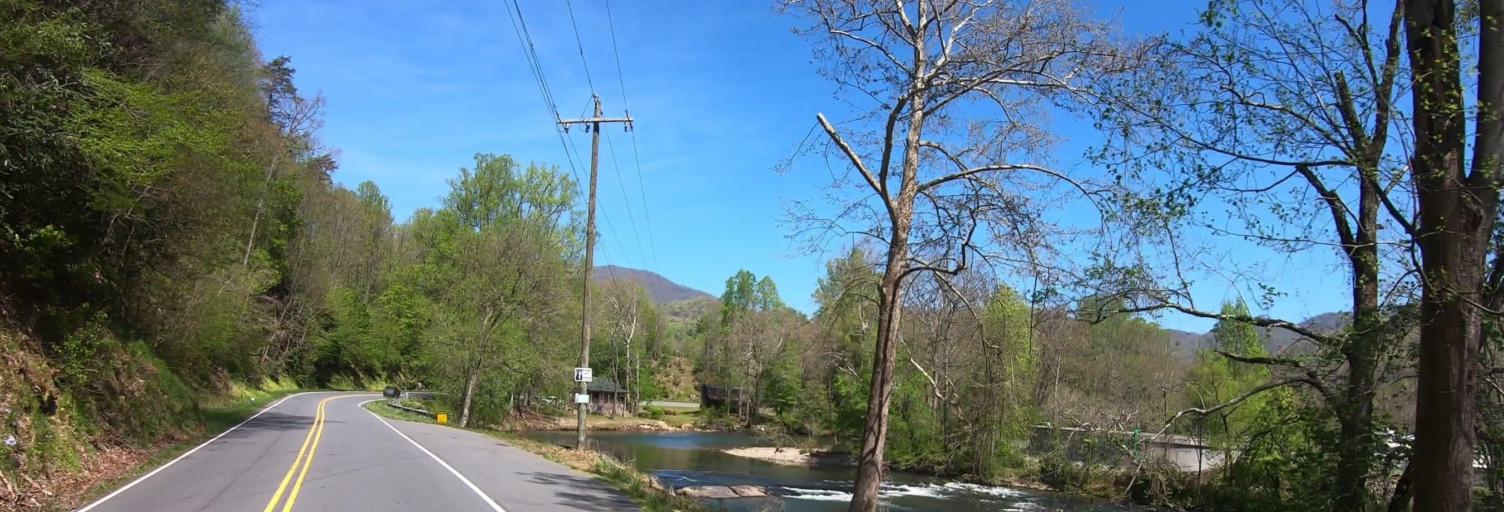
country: US
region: North Carolina
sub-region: Swain County
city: Cherokee
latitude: 35.4654
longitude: -83.3528
